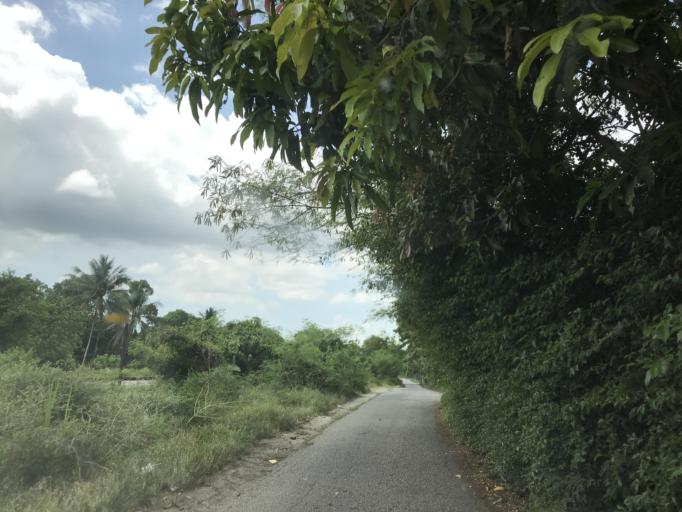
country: MY
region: Kelantan
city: Kota Bharu
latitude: 6.1108
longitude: 102.1925
